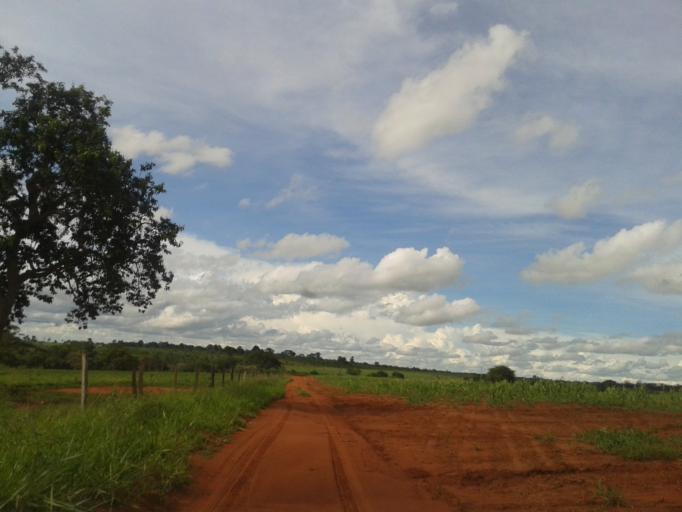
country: BR
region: Minas Gerais
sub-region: Santa Vitoria
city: Santa Vitoria
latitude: -19.1384
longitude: -50.4866
